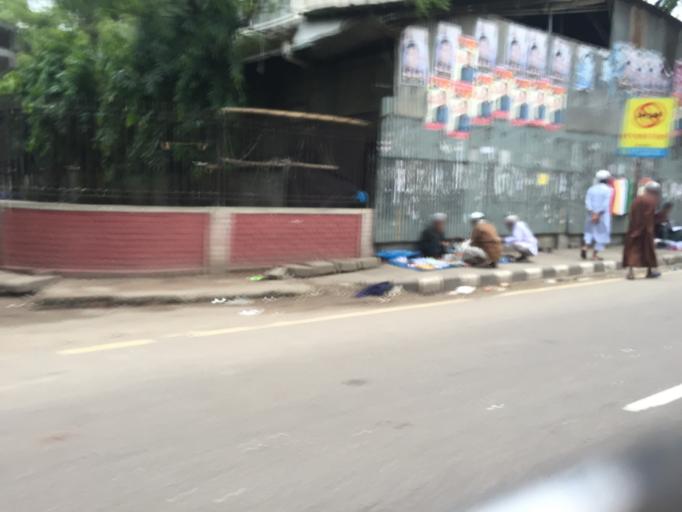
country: BD
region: Dhaka
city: Paltan
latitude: 23.7361
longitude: 90.4038
